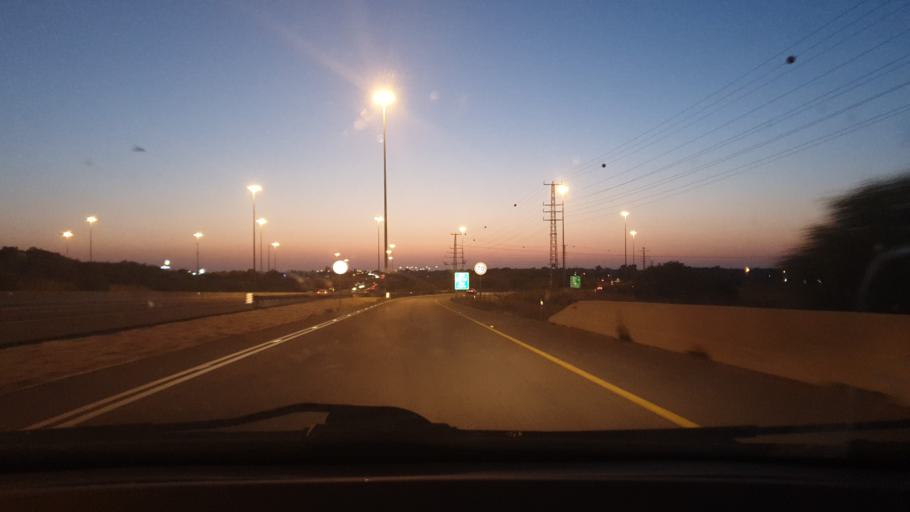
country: IL
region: Central District
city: Gedera
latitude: 31.8029
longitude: 34.7696
